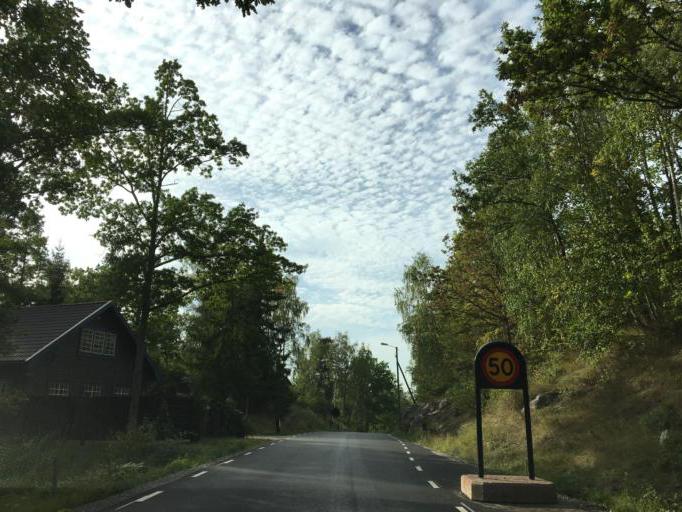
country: SE
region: Soedermanland
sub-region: Eskilstuna Kommun
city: Torshalla
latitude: 59.4502
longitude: 16.4399
